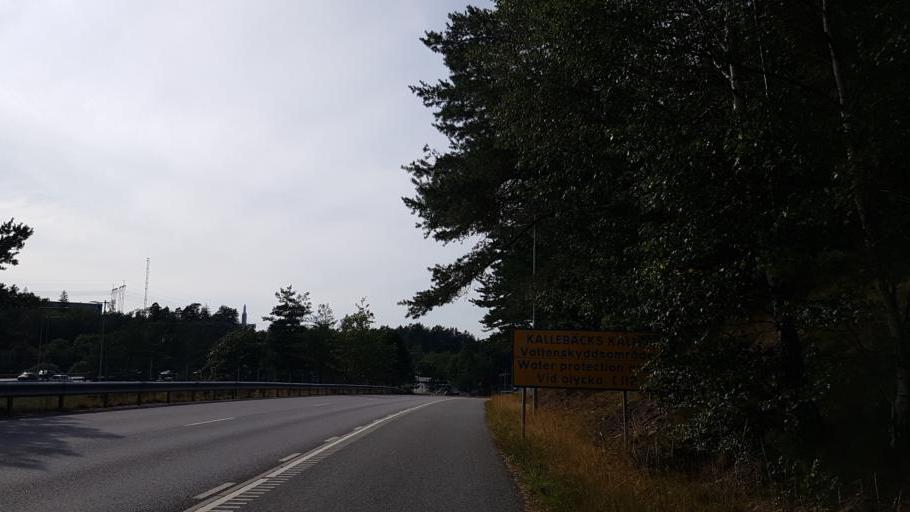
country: SE
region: Vaestra Goetaland
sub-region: Molndal
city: Moelndal
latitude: 57.6766
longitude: 12.0300
